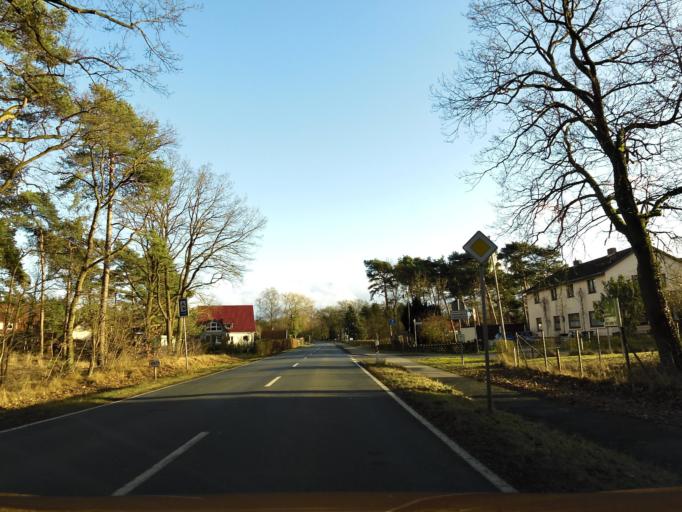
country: DE
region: Lower Saxony
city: Essel
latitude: 52.6895
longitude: 9.6975
